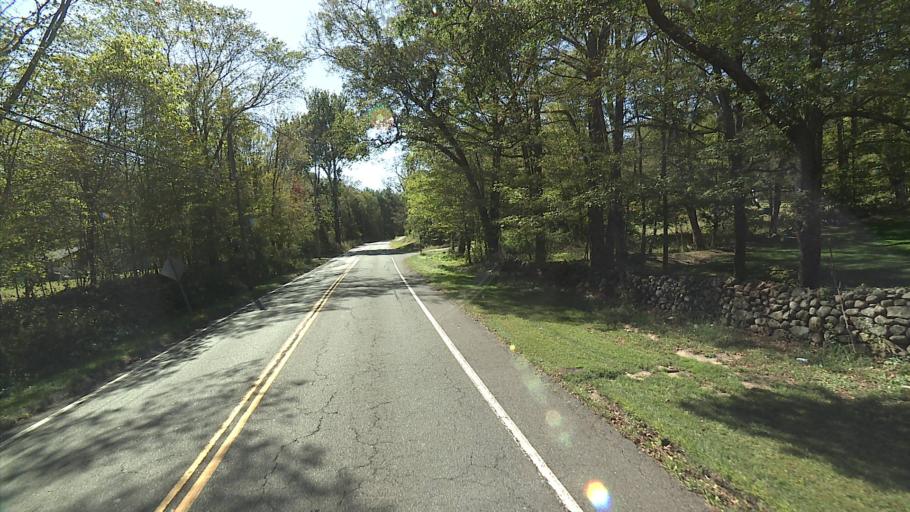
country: US
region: Connecticut
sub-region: New Haven County
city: Woodbridge
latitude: 41.3584
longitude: -72.9835
